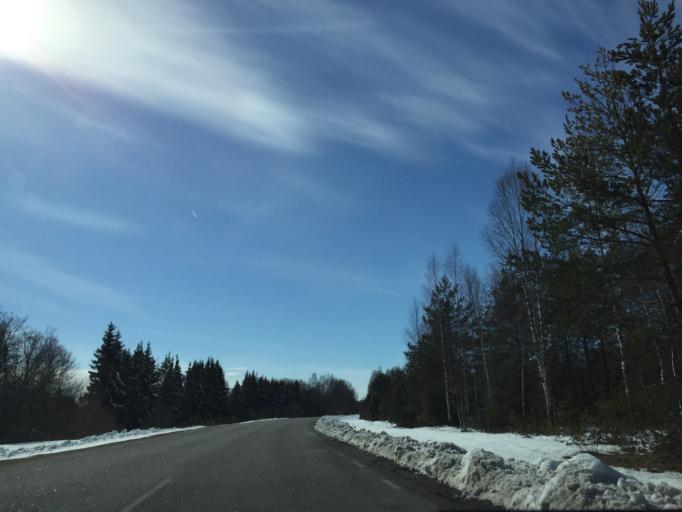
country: EE
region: Saare
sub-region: Orissaare vald
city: Orissaare
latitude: 58.4004
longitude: 22.9904
